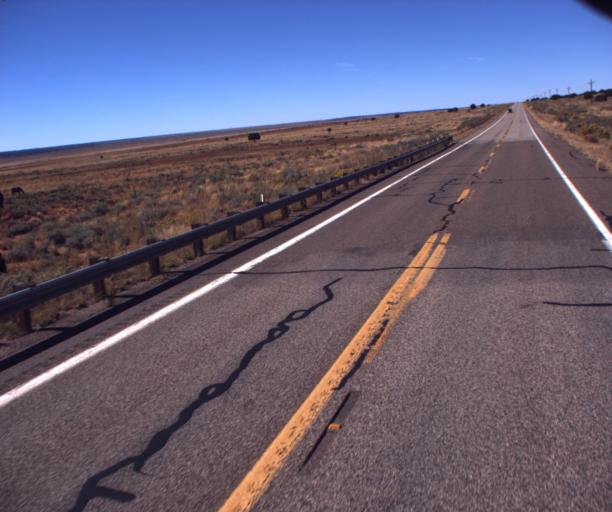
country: US
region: Arizona
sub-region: Mohave County
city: Colorado City
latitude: 36.8581
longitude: -112.7792
